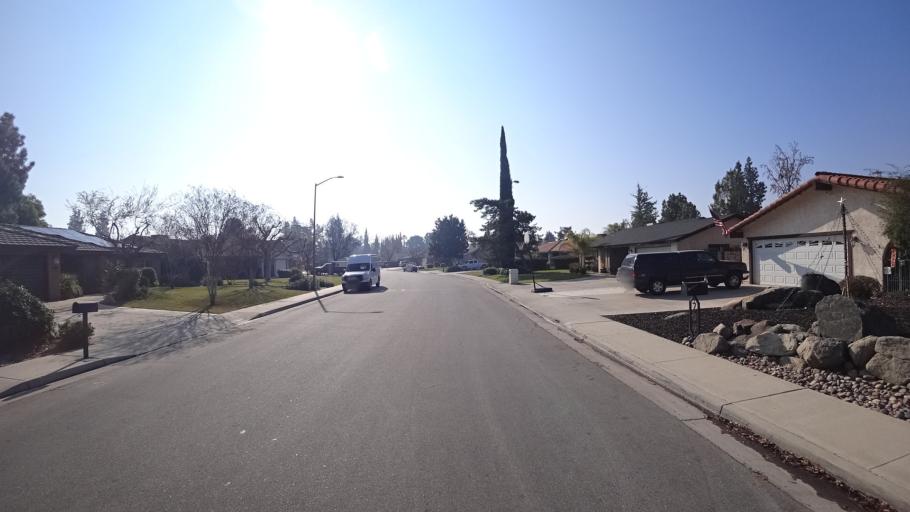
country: US
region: California
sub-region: Kern County
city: Greenacres
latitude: 35.3602
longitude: -119.0858
